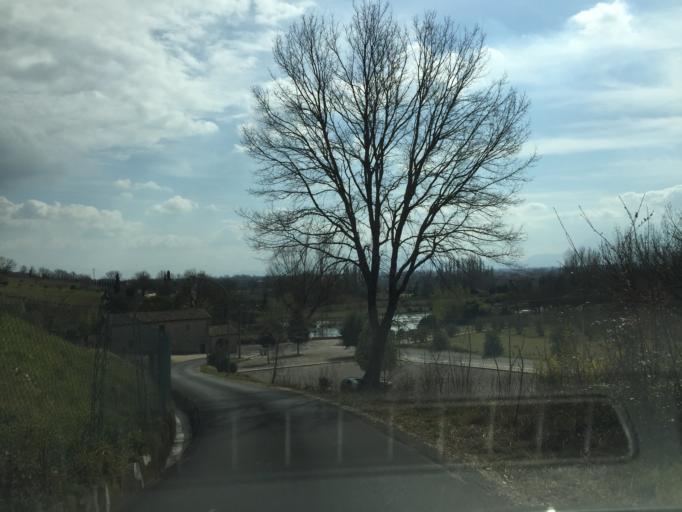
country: IT
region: Latium
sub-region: Provincia di Frosinone
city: Castrocielo
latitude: 41.5203
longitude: 13.7072
